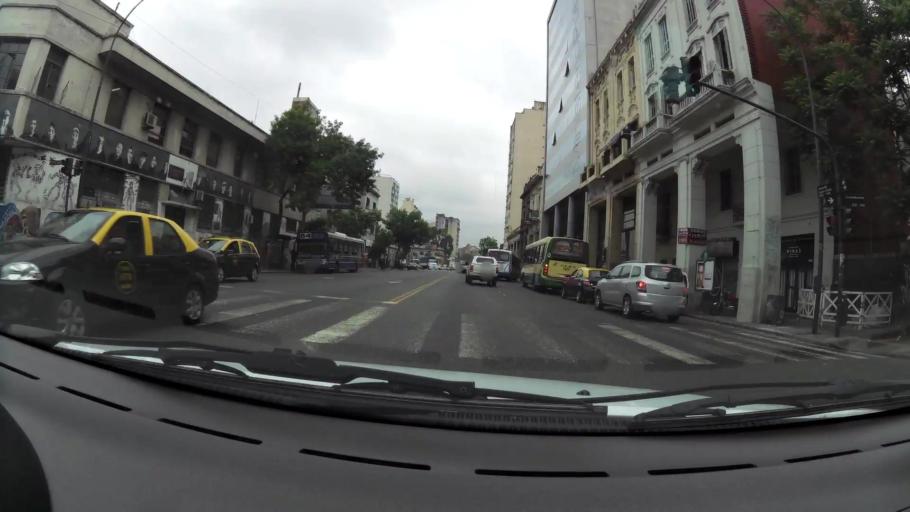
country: AR
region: Buenos Aires F.D.
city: Buenos Aires
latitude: -34.6229
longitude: -58.3682
